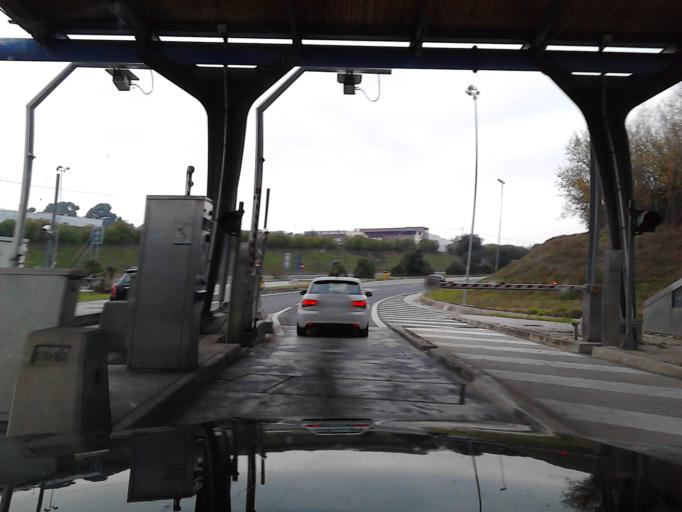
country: IT
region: Abruzzo
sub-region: Provincia di Teramo
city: Villa Rosa
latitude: 42.8357
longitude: 13.9021
